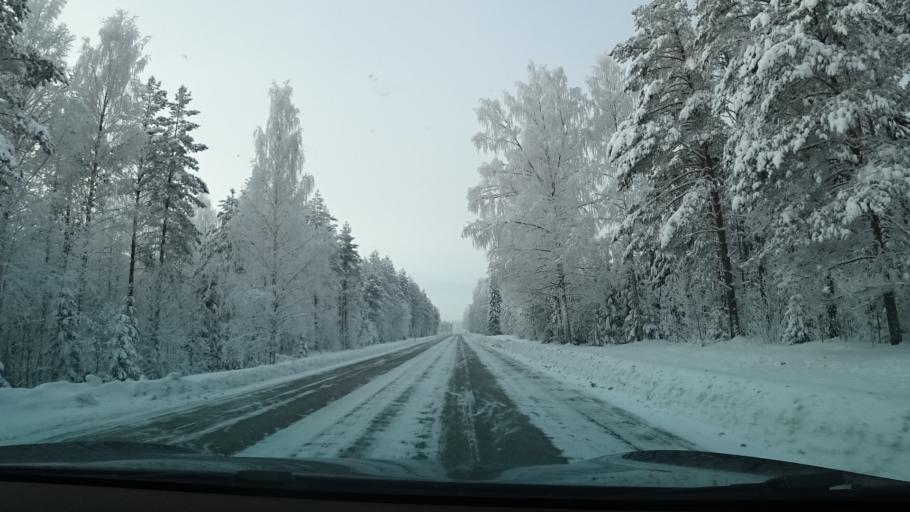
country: FI
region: South Karelia
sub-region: Imatra
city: Saari
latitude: 61.7814
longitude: 29.7076
